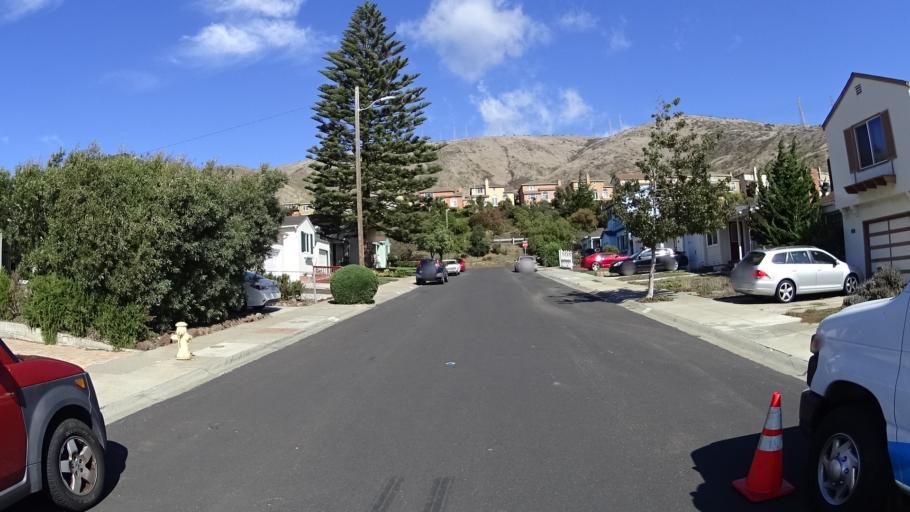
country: US
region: California
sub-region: San Mateo County
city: South San Francisco
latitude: 37.6664
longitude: -122.4105
